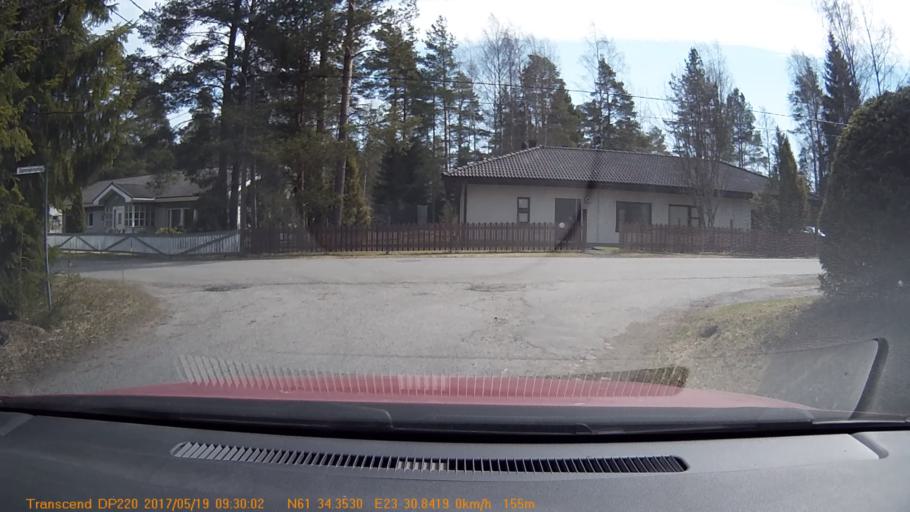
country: FI
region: Pirkanmaa
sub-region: Tampere
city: Yloejaervi
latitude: 61.5725
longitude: 23.5140
